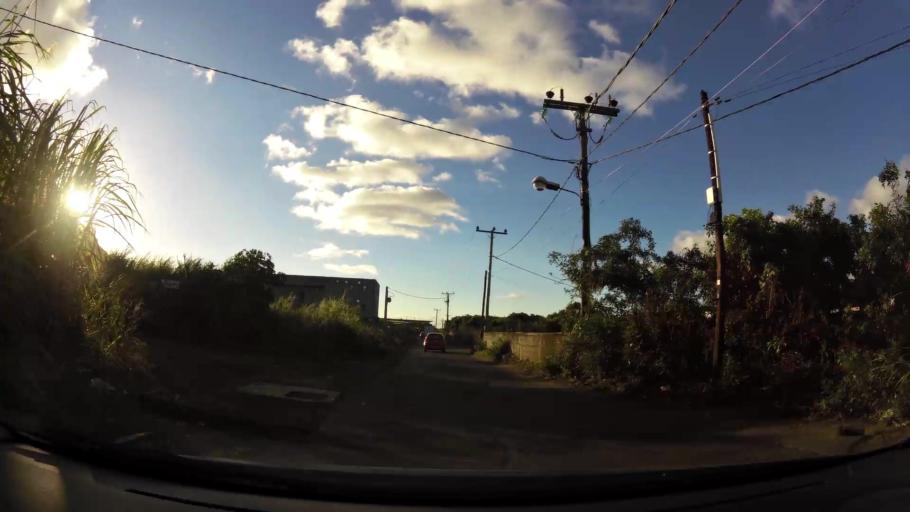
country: MU
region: Plaines Wilhems
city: Quatre Bornes
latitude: -20.2609
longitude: 57.4621
